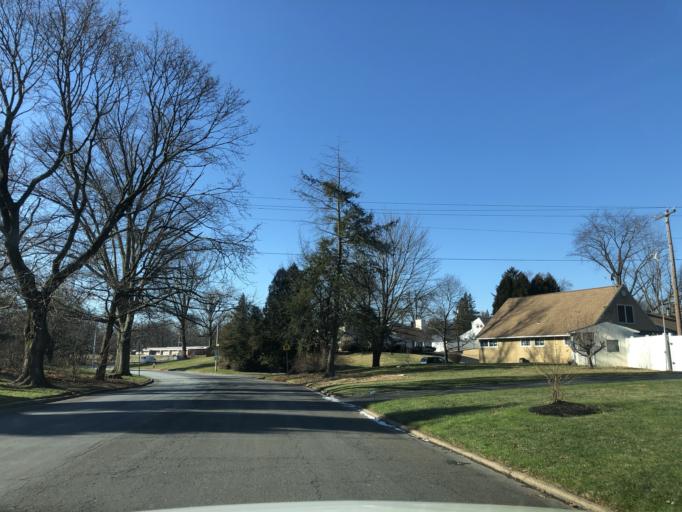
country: US
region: Pennsylvania
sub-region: Bucks County
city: Hulmeville
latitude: 40.1566
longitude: -74.8802
